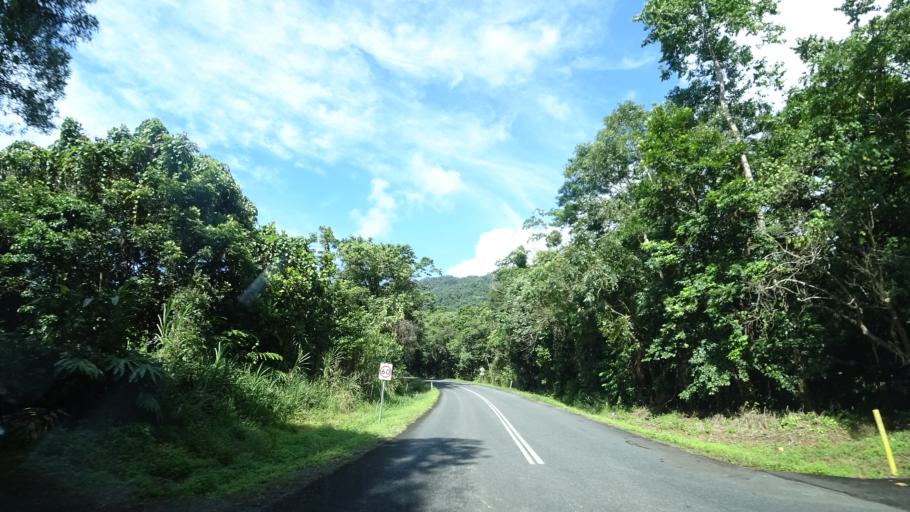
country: AU
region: Queensland
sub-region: Cairns
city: Port Douglas
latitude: -16.1406
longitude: 145.4305
